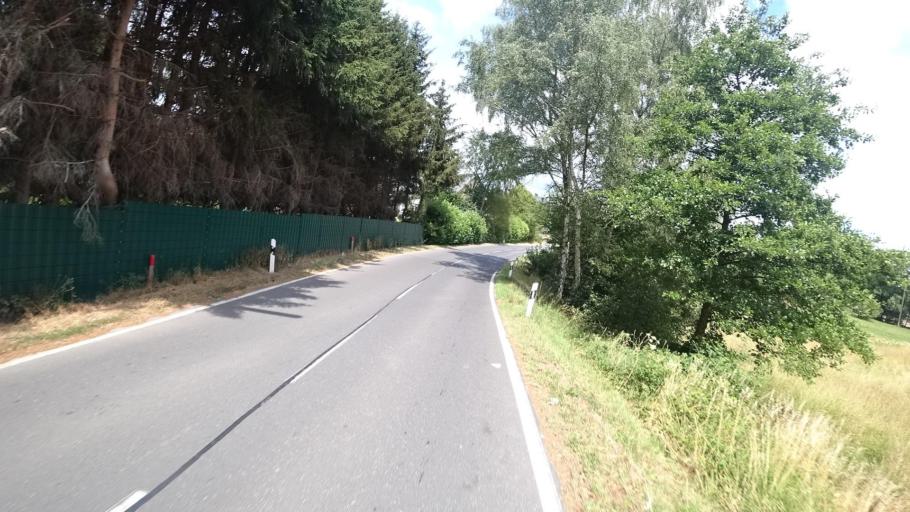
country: DE
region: Rheinland-Pfalz
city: Oberirsen
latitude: 50.7210
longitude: 7.5681
